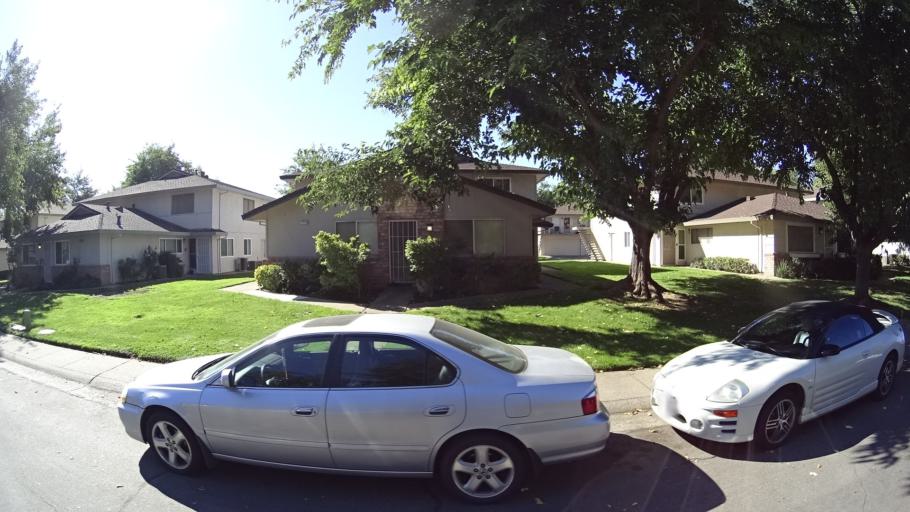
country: US
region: California
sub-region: Sacramento County
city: Elk Grove
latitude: 38.4057
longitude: -121.3697
